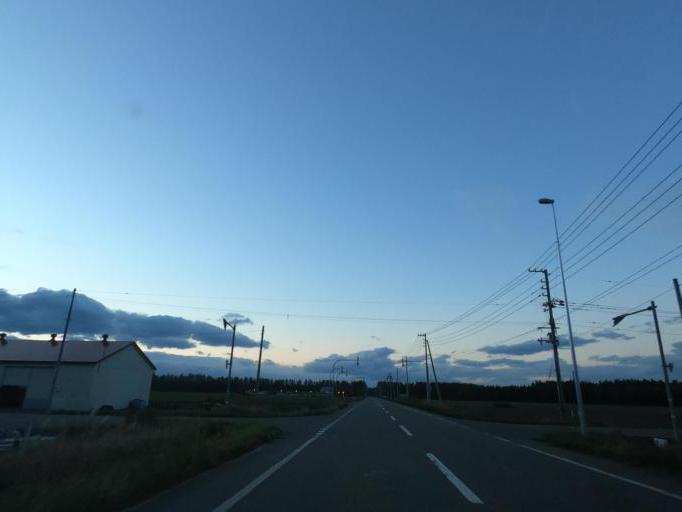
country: JP
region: Hokkaido
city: Obihiro
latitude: 42.6691
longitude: 143.1725
